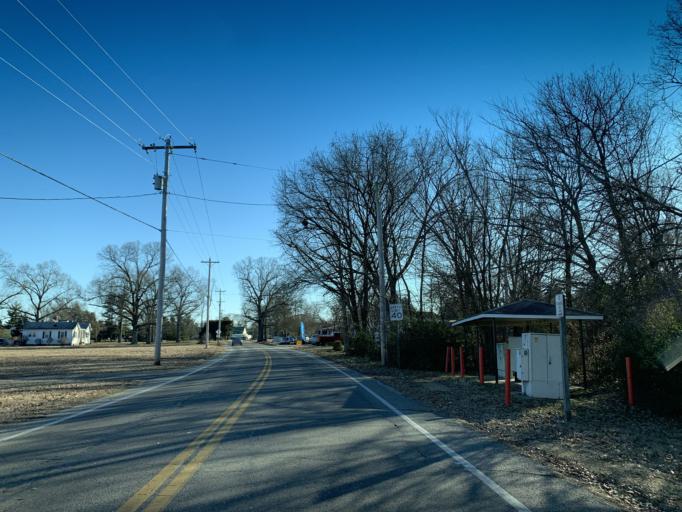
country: US
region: Maryland
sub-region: Saint Mary's County
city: Charlotte Hall
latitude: 38.5000
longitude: -76.7771
